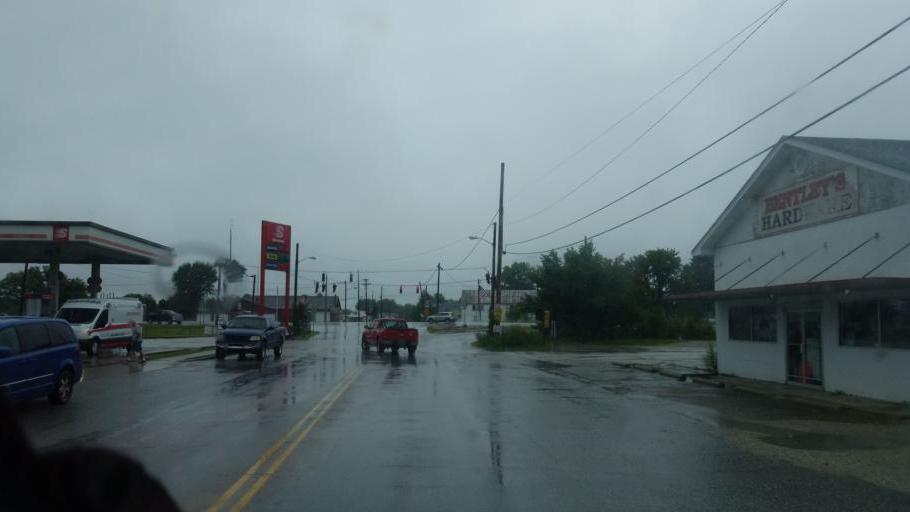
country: US
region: Kentucky
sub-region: Greenup County
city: South Shore
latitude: 38.7201
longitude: -82.9639
